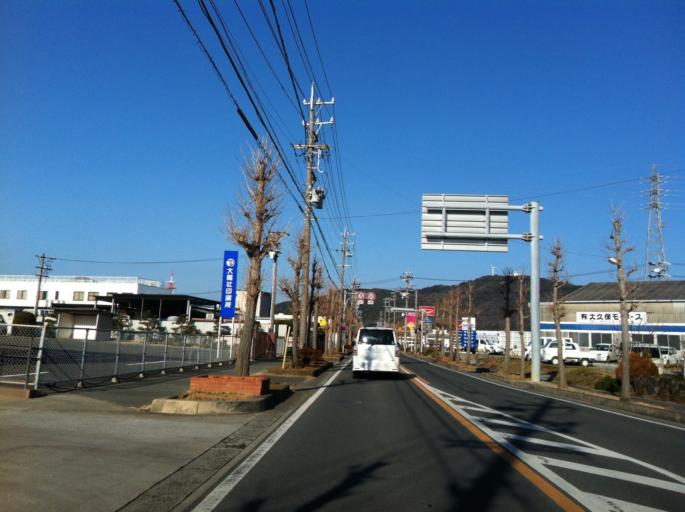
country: JP
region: Aichi
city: Tahara
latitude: 34.6698
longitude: 137.2787
